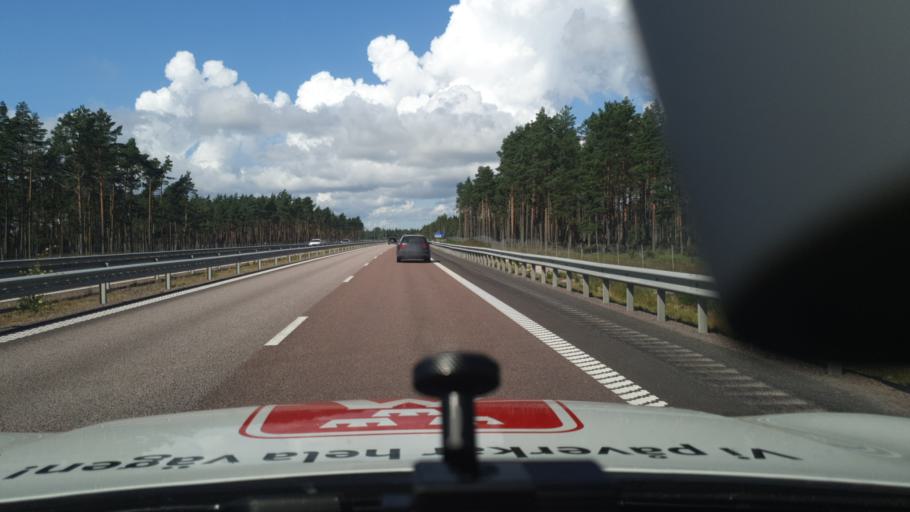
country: SE
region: Vaermland
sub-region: Kils Kommun
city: Kil
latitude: 59.3890
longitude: 13.3007
